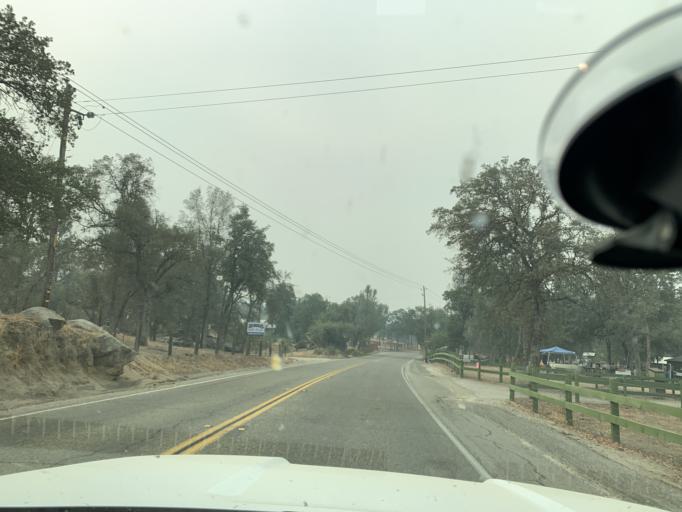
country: US
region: California
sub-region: Fresno County
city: Auberry
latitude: 37.0538
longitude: -119.4973
